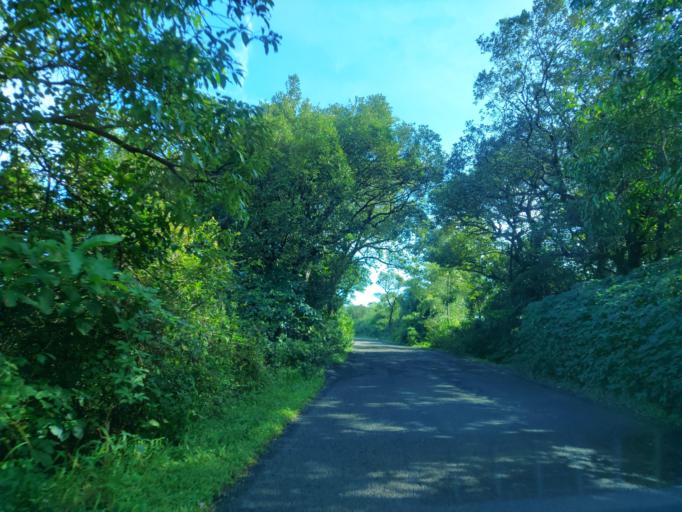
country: IN
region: Maharashtra
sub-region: Kolhapur
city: Ajra
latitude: 16.0118
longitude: 74.0489
